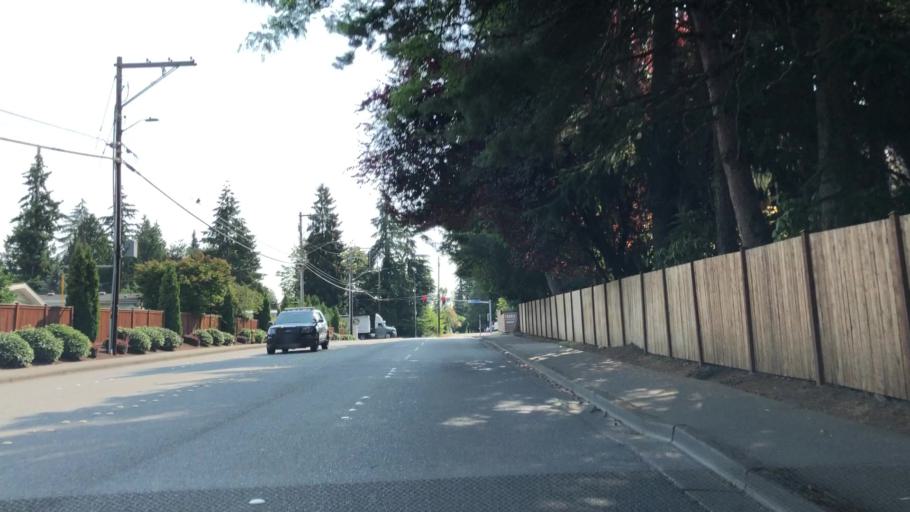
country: US
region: Washington
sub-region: Snohomish County
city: Alderwood Manor
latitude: 47.8391
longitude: -122.2944
